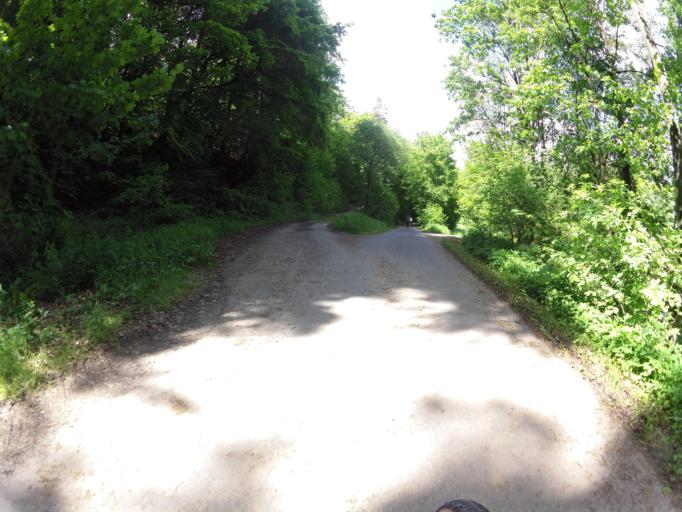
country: DE
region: Thuringia
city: Ebenshausen
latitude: 51.0884
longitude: 10.3034
